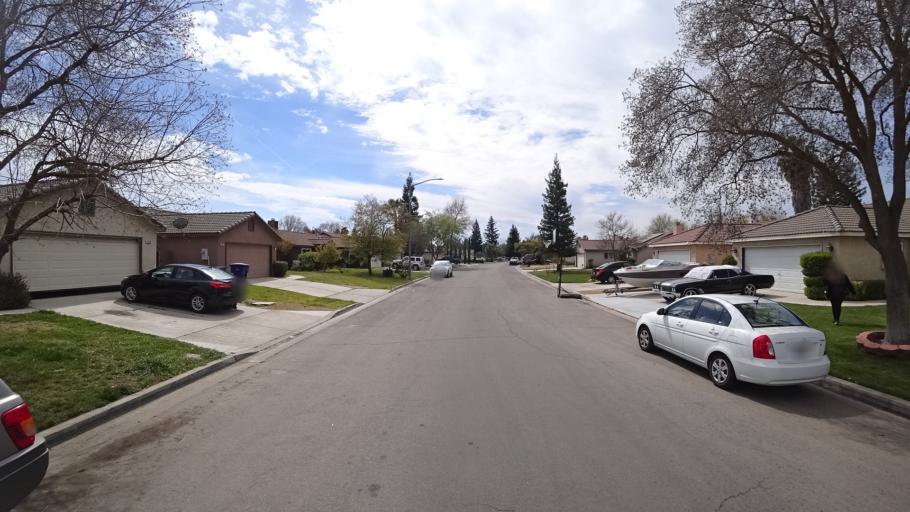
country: US
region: California
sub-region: Fresno County
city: West Park
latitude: 36.8186
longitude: -119.8862
